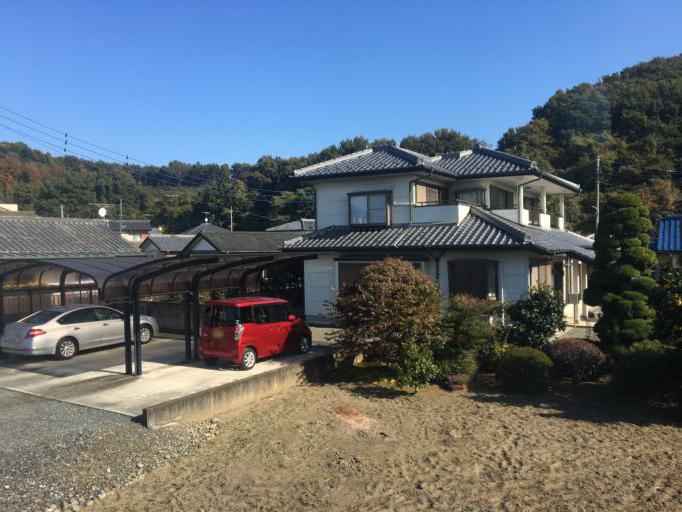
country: JP
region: Gunma
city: Kiryu
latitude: 36.3775
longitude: 139.3715
